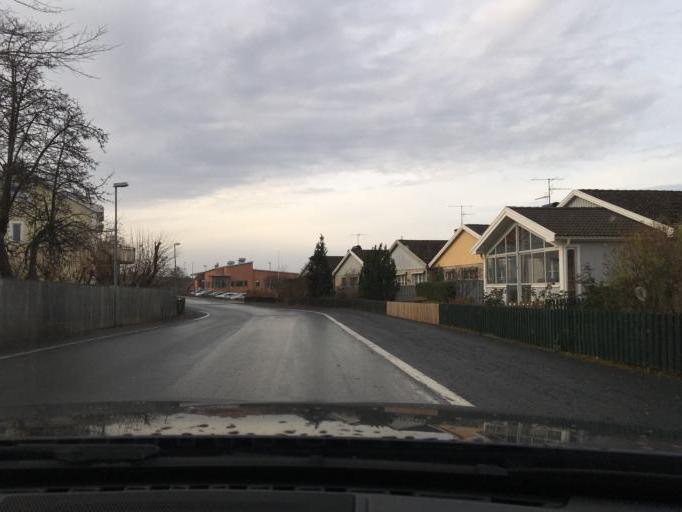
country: SE
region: Joenkoeping
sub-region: Jonkopings Kommun
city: Graenna
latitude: 58.0248
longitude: 14.4655
